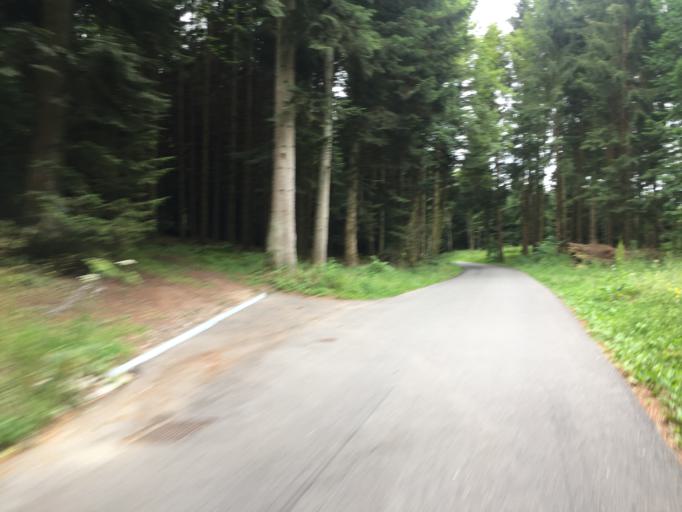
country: CH
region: Bern
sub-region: Bern-Mittelland District
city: Stettlen
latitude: 46.9466
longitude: 7.5224
